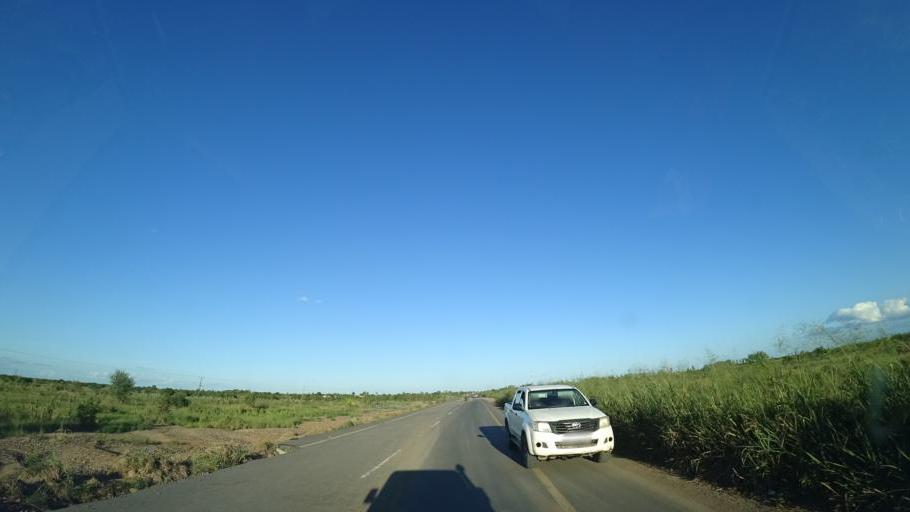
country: MZ
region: Sofala
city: Dondo
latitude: -19.3257
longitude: 34.3039
